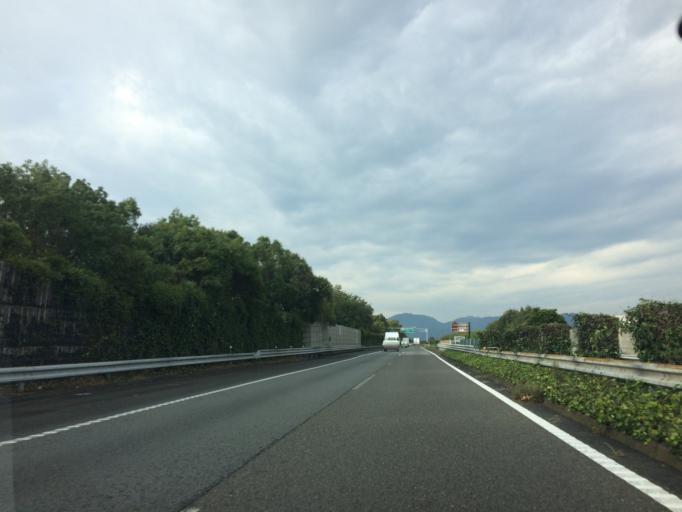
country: JP
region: Shizuoka
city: Shizuoka-shi
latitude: 34.9588
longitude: 138.4179
